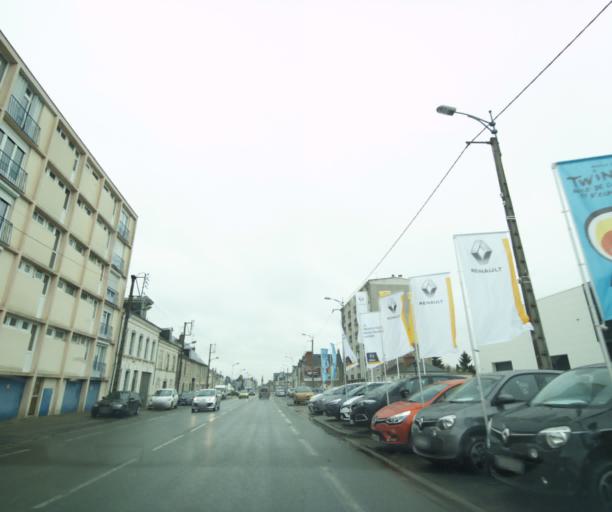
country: FR
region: Centre
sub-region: Departement du Loiret
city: Saran
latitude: 47.9359
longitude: 1.8945
